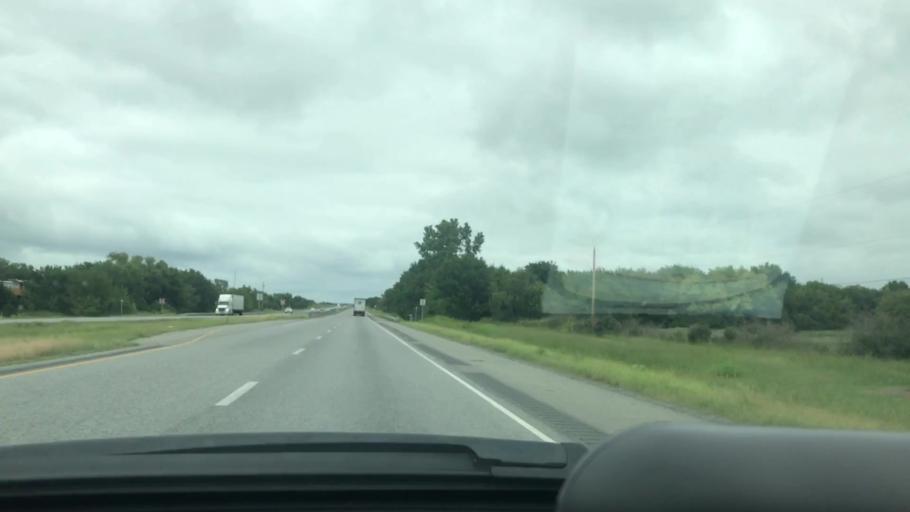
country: US
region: Oklahoma
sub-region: Pittsburg County
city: McAlester
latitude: 34.7403
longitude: -95.8980
